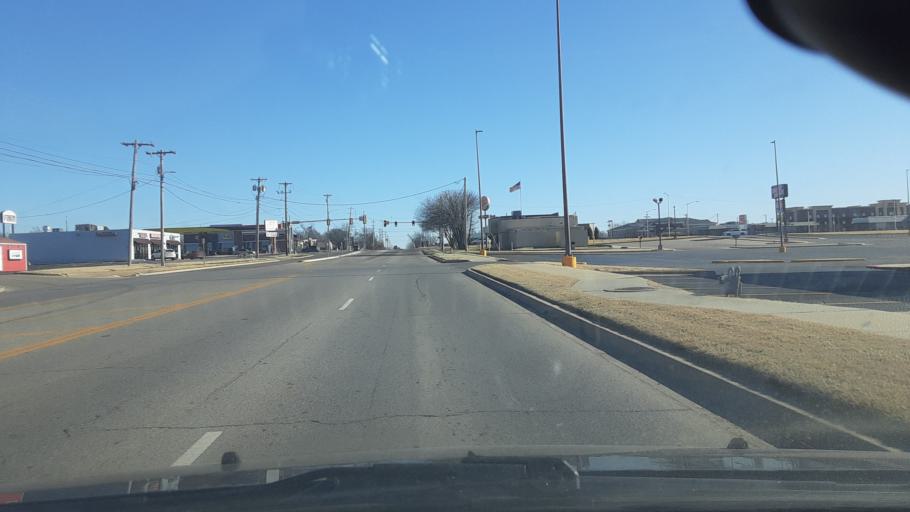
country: US
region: Oklahoma
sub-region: Kay County
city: Ponca City
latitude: 36.7385
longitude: -97.0692
